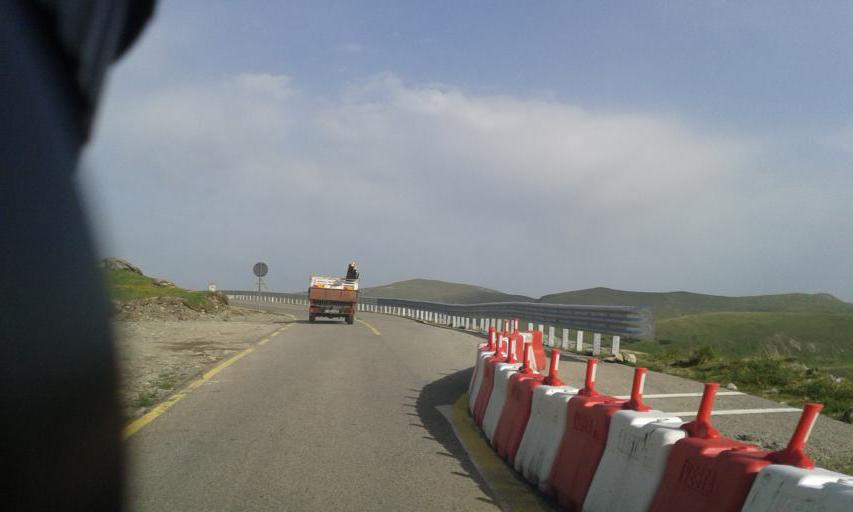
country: RO
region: Gorj
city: Novaci-Straini
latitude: 45.3596
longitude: 23.6620
